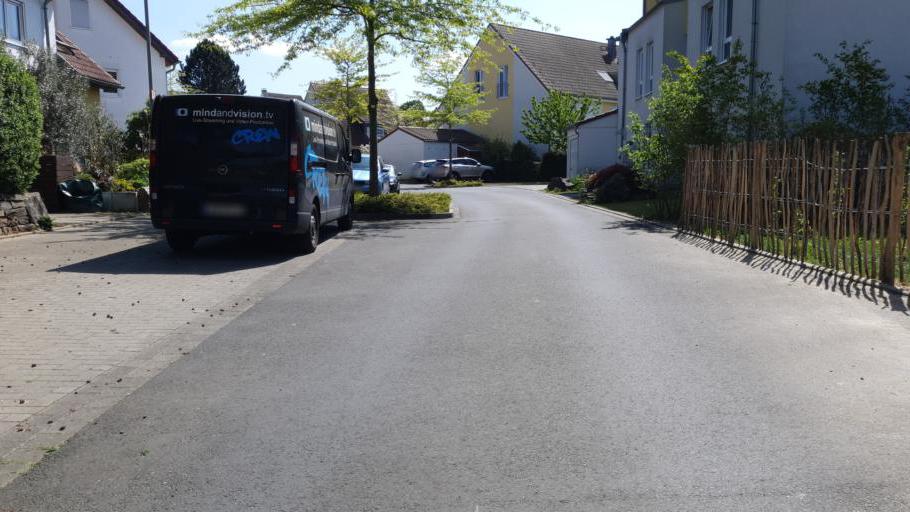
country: DE
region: North Rhine-Westphalia
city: Opladen
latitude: 51.0444
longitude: 7.0484
